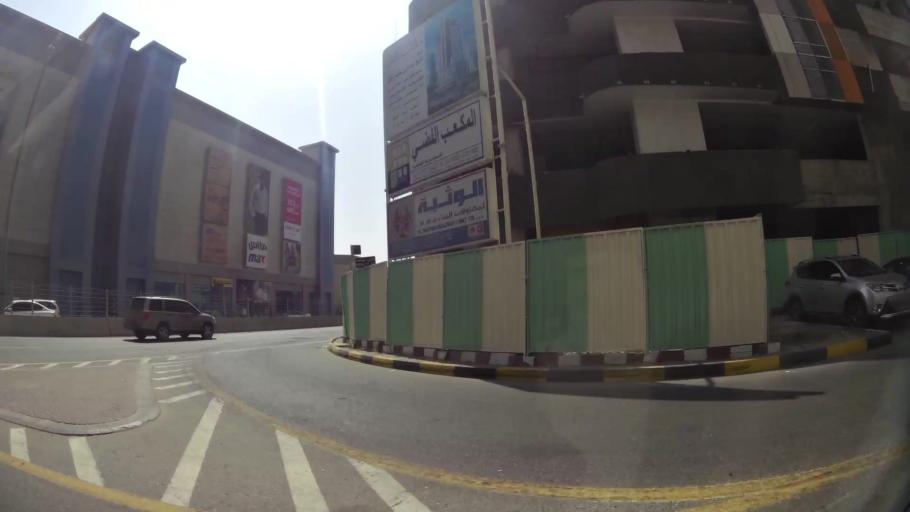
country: AE
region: Ash Shariqah
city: Sharjah
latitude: 25.3088
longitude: 55.3786
